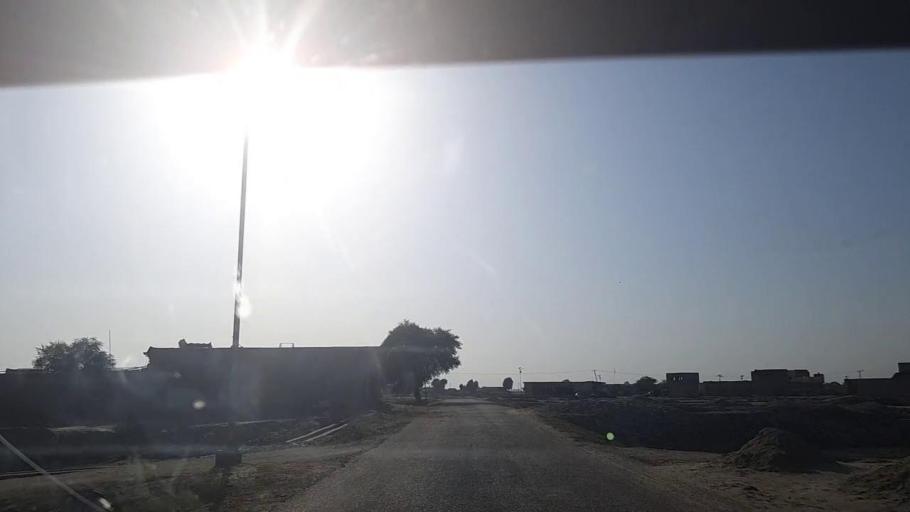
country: PK
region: Sindh
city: Tangwani
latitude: 28.2617
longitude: 69.0047
